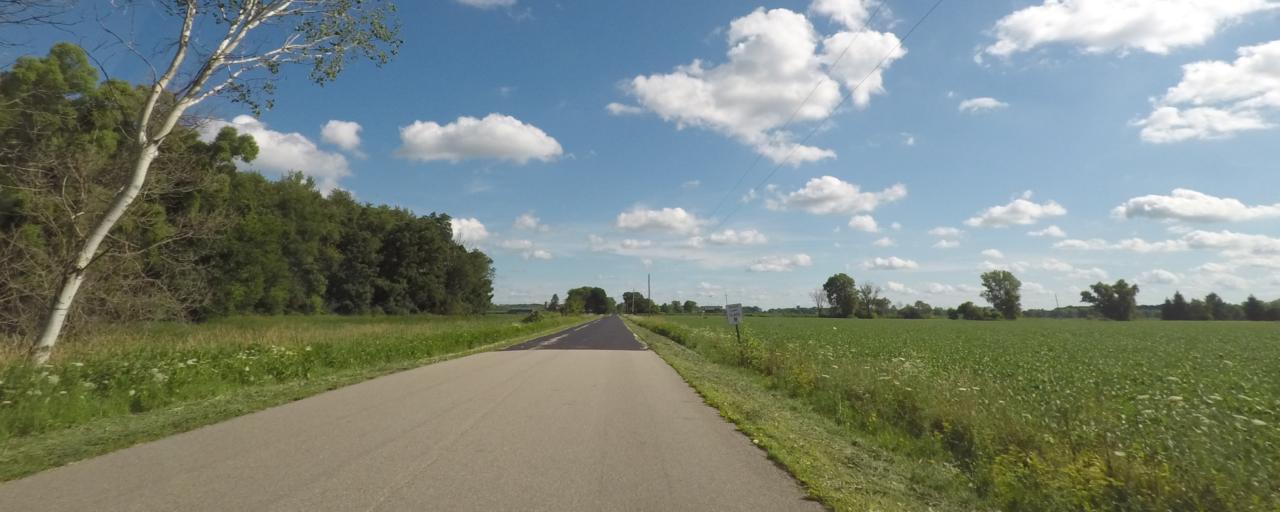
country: US
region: Wisconsin
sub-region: Rock County
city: Edgerton
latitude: 42.8911
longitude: -89.1321
